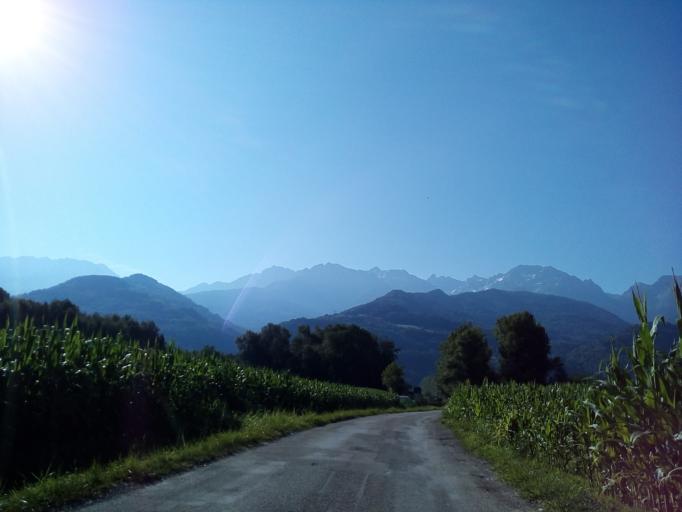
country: FR
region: Rhone-Alpes
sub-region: Departement de l'Isere
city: Saint-Nazaire-les-Eymes
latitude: 45.2526
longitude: 5.8718
